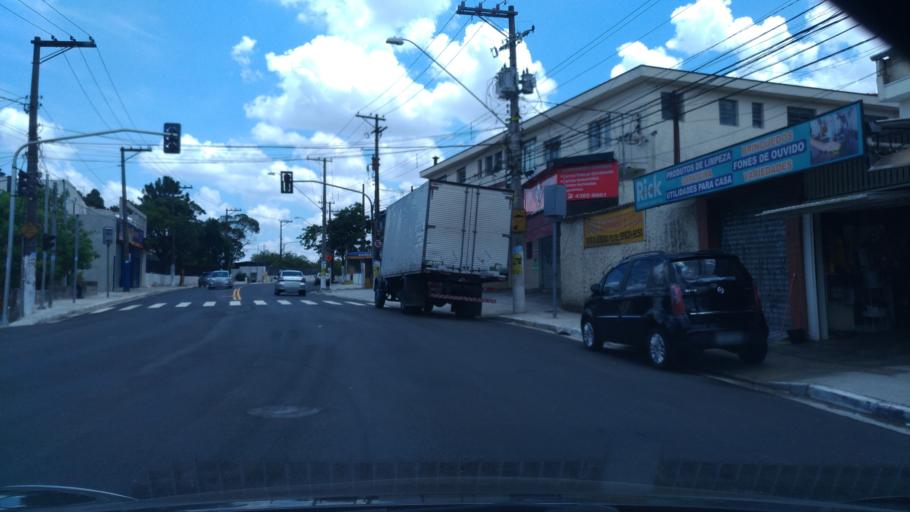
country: BR
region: Sao Paulo
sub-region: Sao Bernardo Do Campo
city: Sao Bernardo do Campo
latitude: -23.7020
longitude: -46.5878
